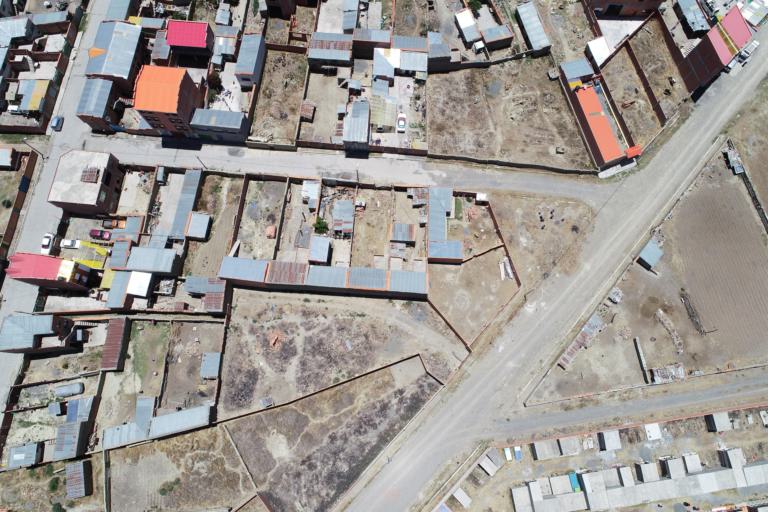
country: BO
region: La Paz
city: Achacachi
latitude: -16.0466
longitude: -68.6891
